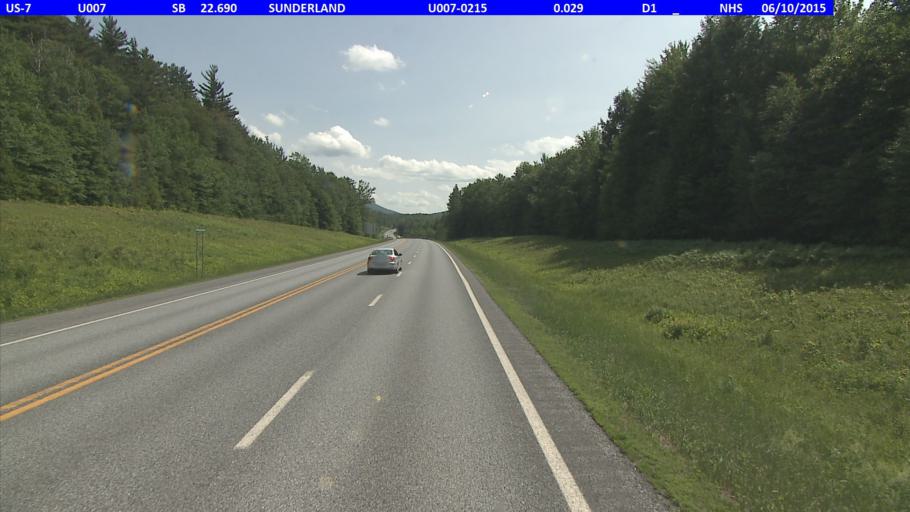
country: US
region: Vermont
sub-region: Bennington County
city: Arlington
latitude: 43.0263
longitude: -73.1400
